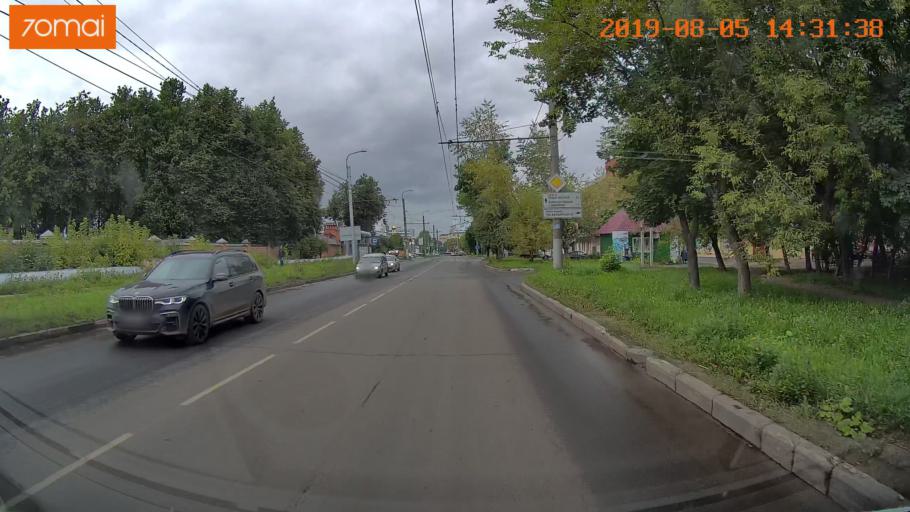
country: RU
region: Ivanovo
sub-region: Gorod Ivanovo
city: Ivanovo
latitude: 56.9879
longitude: 40.9994
